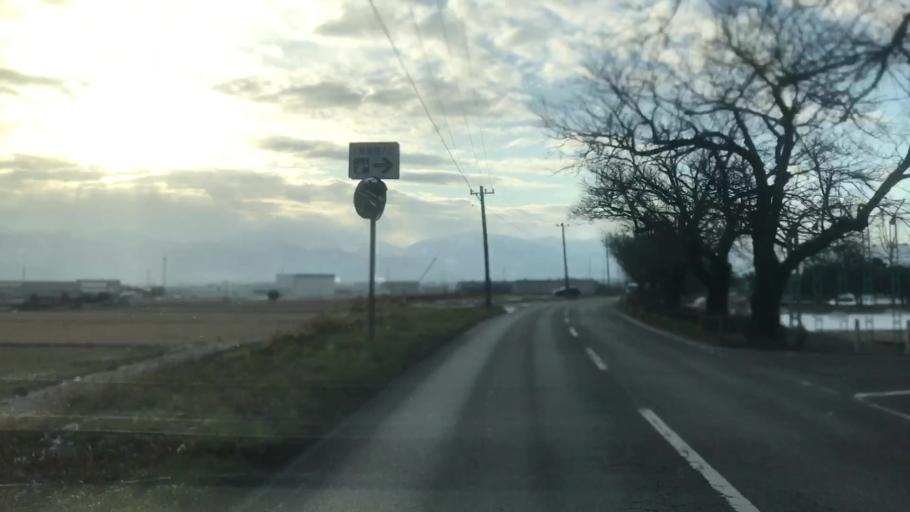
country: JP
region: Toyama
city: Toyama-shi
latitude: 36.7012
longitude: 137.2809
